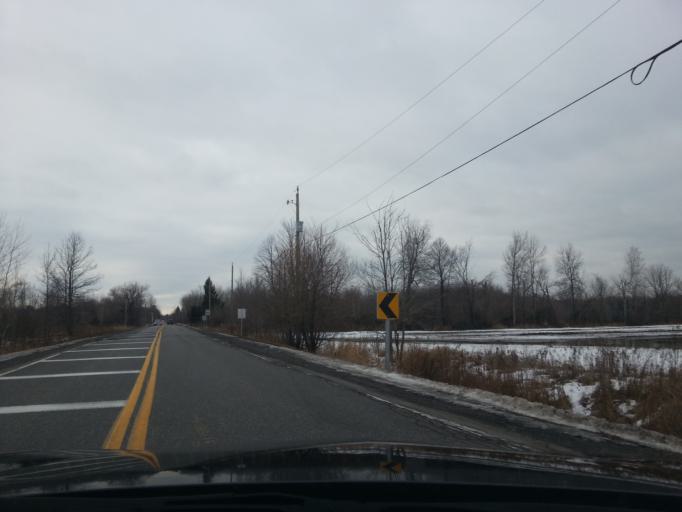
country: CA
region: Ontario
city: Ottawa
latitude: 45.4242
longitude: -75.5422
